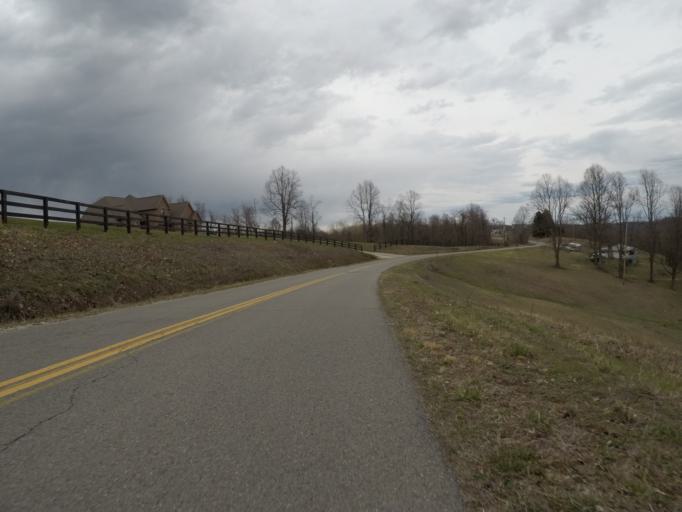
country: US
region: Ohio
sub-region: Lawrence County
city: Burlington
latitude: 38.4419
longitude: -82.5274
